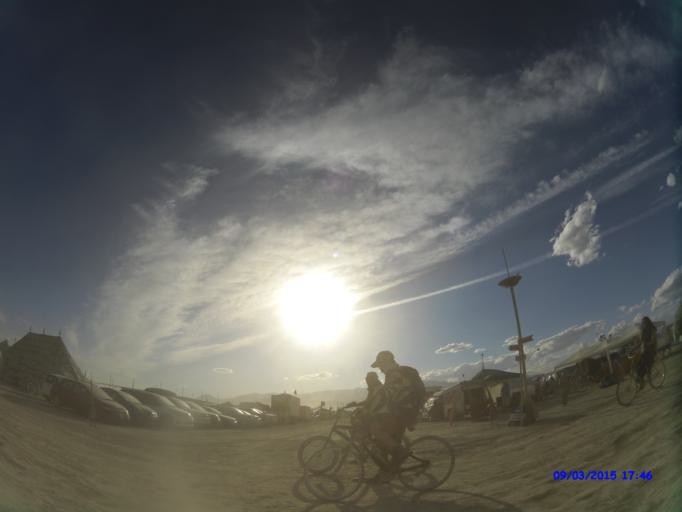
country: US
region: Nevada
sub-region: Pershing County
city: Lovelock
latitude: 40.7750
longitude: -119.2065
